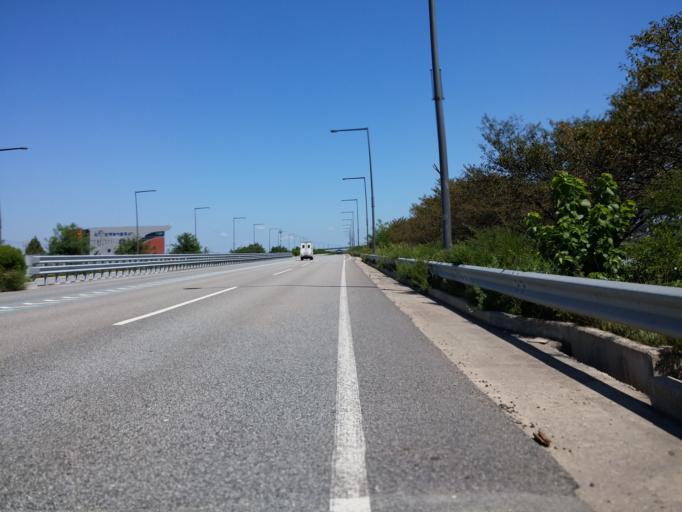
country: KR
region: Chungcheongbuk-do
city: Cheongju-si
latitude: 36.5934
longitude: 127.3299
